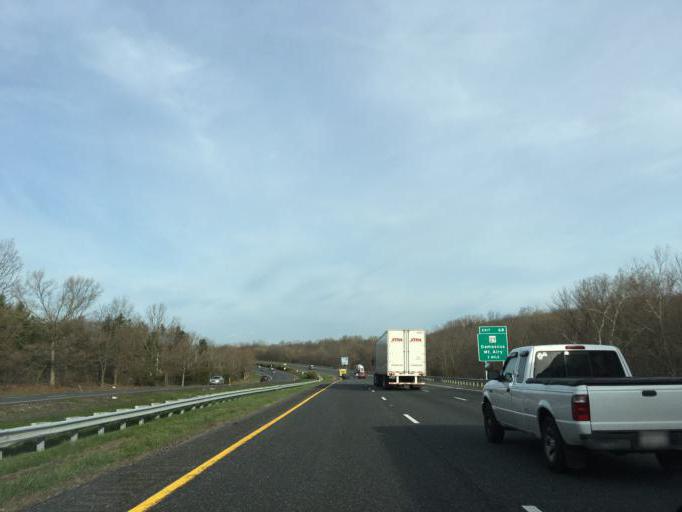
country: US
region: Maryland
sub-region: Carroll County
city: Mount Airy
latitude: 39.3589
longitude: -77.1421
